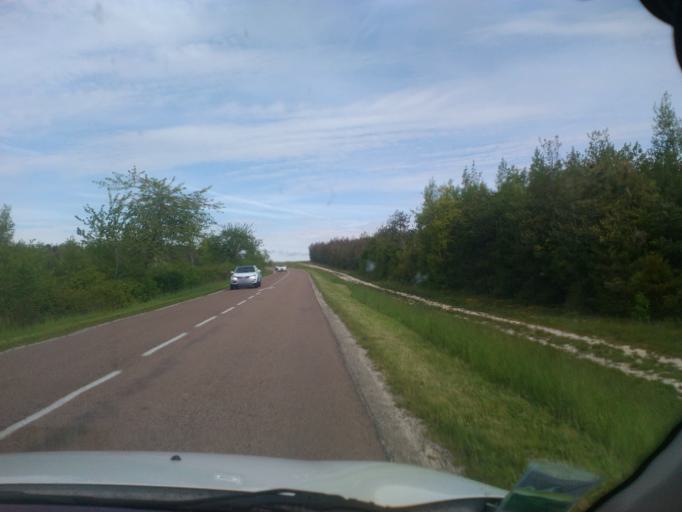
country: FR
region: Champagne-Ardenne
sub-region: Departement de l'Aube
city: Payns
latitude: 48.3799
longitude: 3.8732
